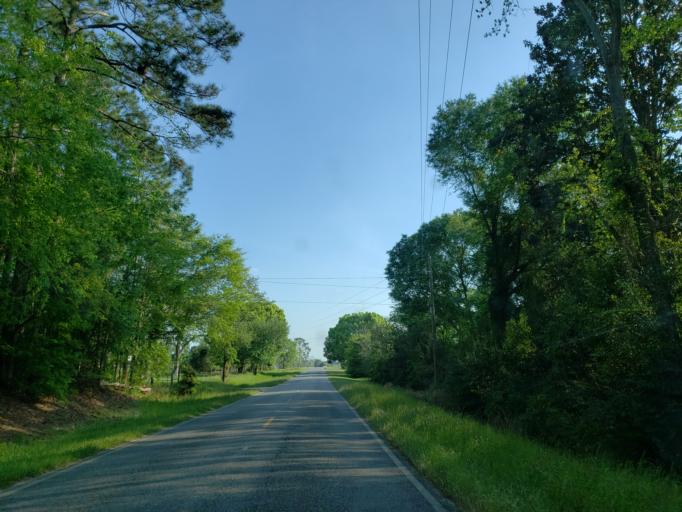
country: US
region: Georgia
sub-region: Tift County
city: Tifton
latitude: 31.5067
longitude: -83.5602
